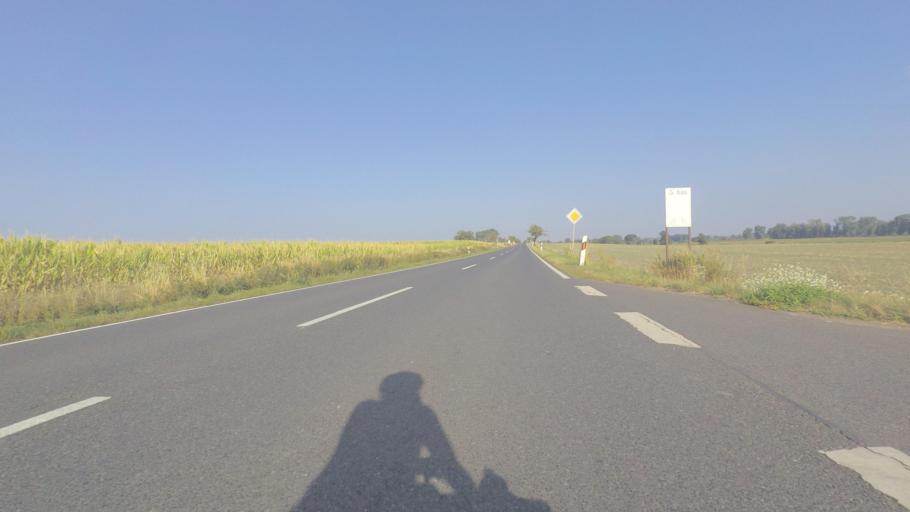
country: DE
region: Brandenburg
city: Kremmen
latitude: 52.7522
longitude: 12.9007
